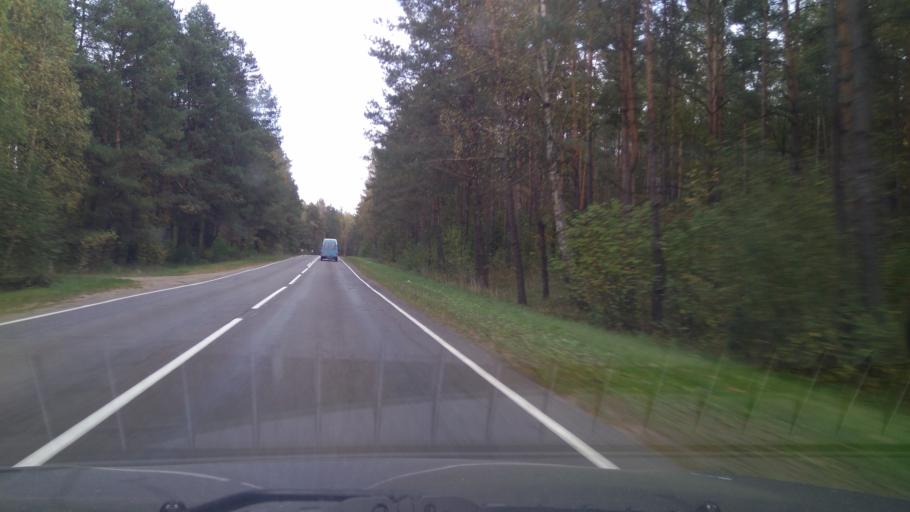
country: BY
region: Minsk
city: Druzhny
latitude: 53.6374
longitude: 27.8986
